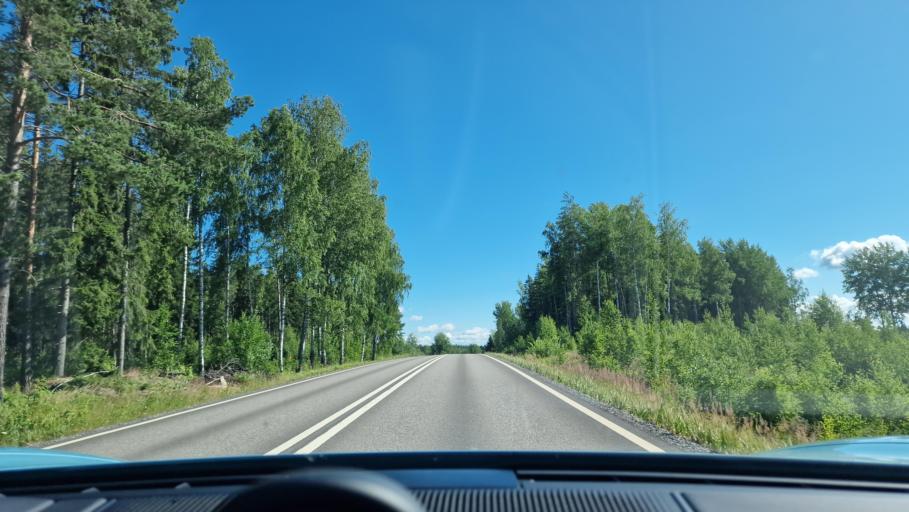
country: FI
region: Pirkanmaa
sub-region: Tampere
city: Kangasala
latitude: 61.5006
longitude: 24.1749
